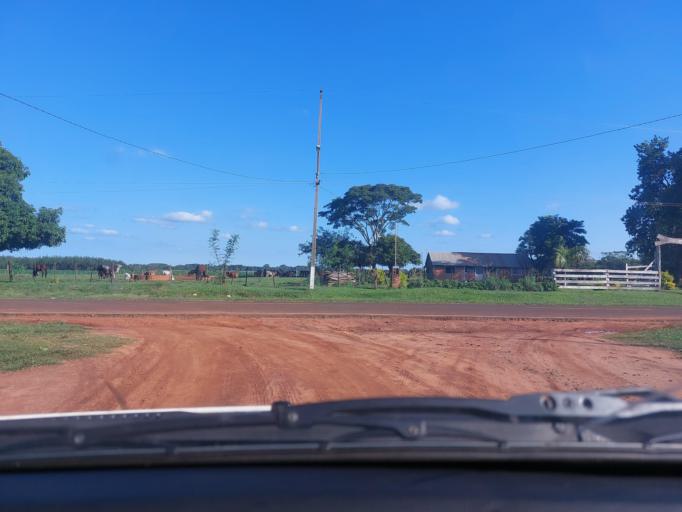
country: PY
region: San Pedro
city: Guayaybi
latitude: -24.5314
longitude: -56.5456
